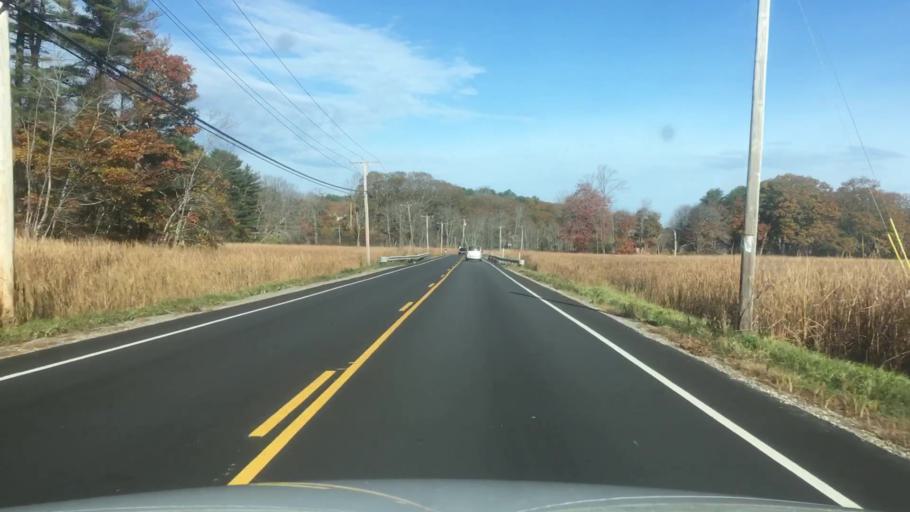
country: US
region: Maine
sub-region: Sagadahoc County
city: Woolwich
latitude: 43.9017
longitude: -69.7968
